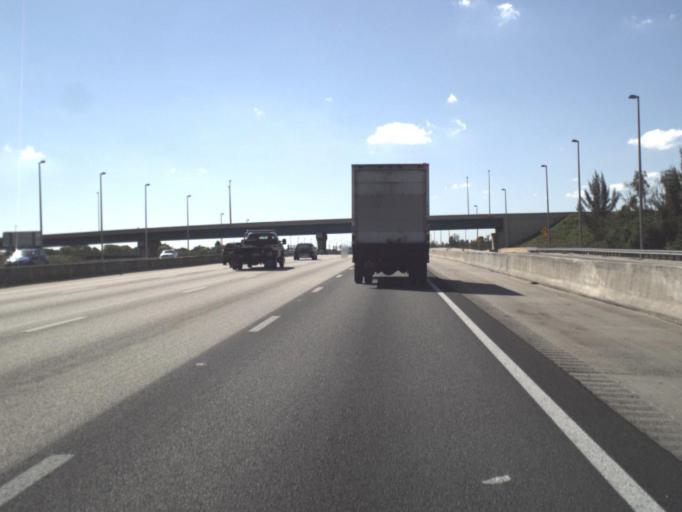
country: US
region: Florida
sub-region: Miami-Dade County
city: Doral
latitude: 25.8424
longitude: -80.3874
